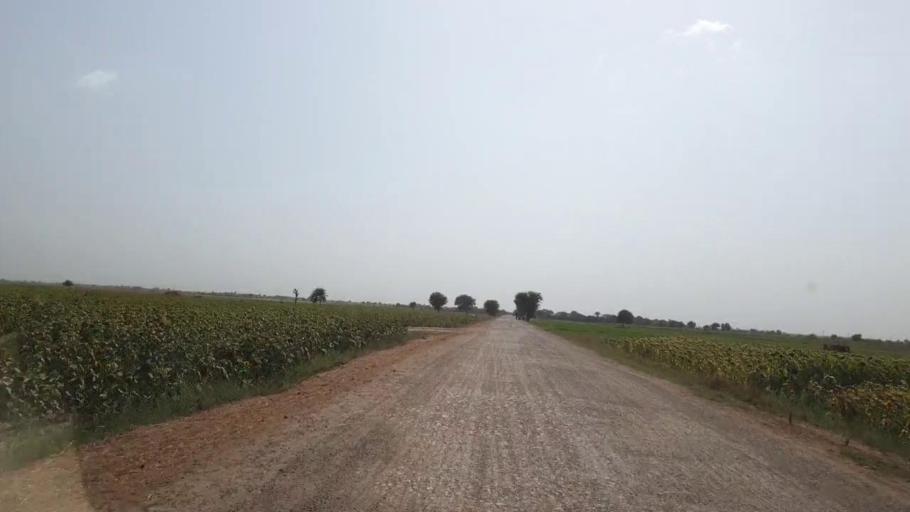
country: PK
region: Sindh
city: Rajo Khanani
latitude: 25.0462
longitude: 68.8765
